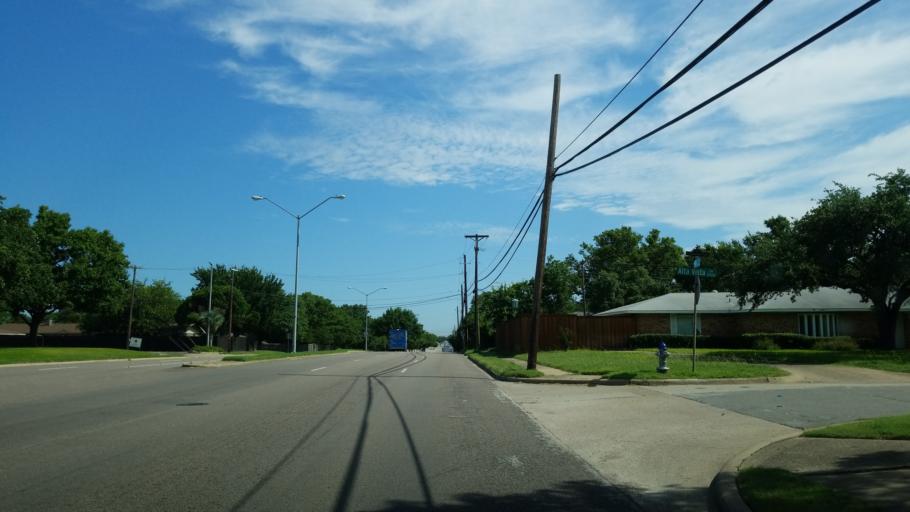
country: US
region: Texas
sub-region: Dallas County
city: Farmers Branch
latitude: 32.9041
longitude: -96.8561
